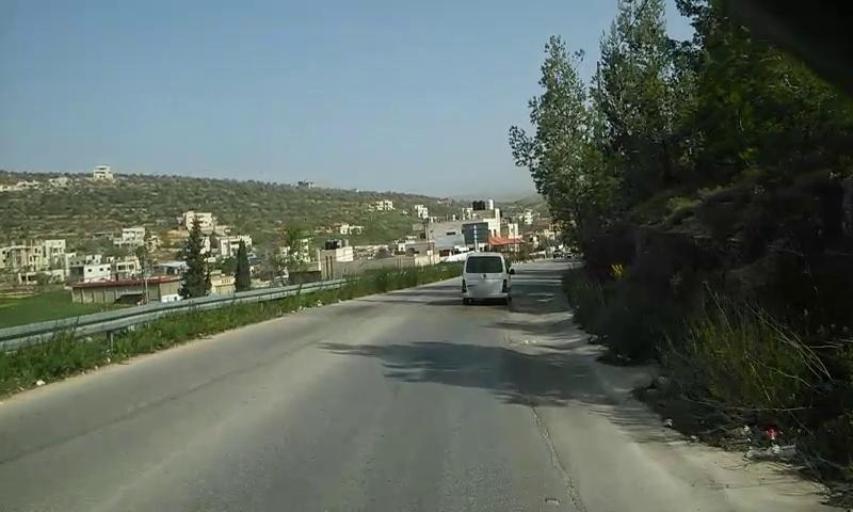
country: PS
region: West Bank
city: Dura al Qar`
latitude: 31.9689
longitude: 35.2273
